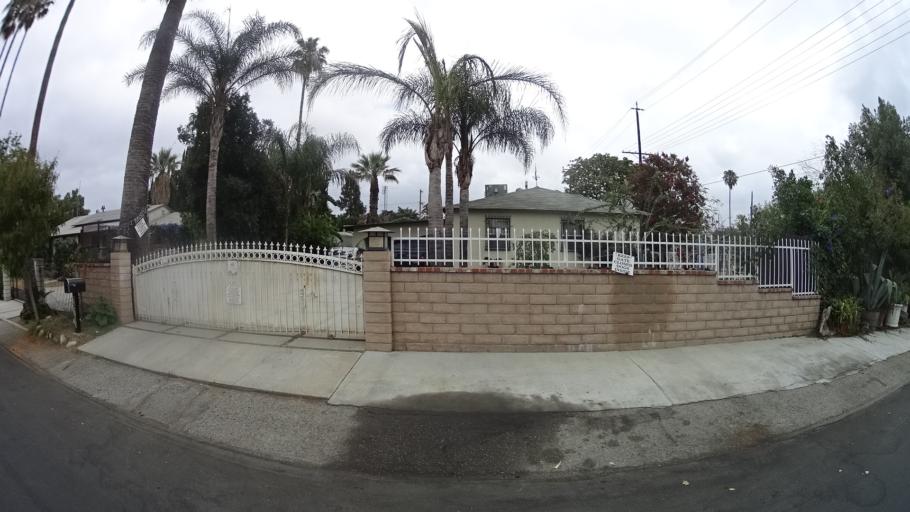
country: US
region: California
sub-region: Los Angeles County
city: San Fernando
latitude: 34.2414
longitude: -118.4538
